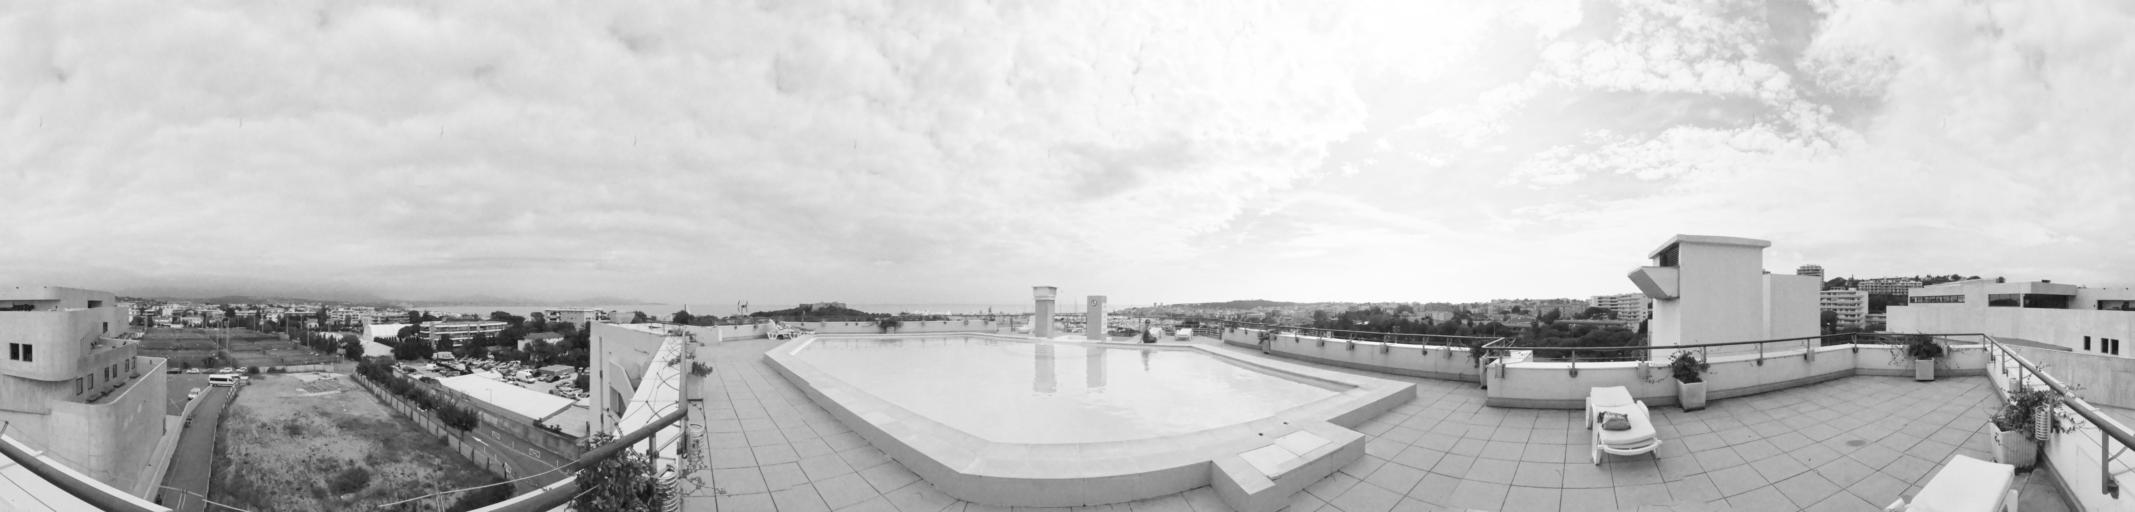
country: FR
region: Provence-Alpes-Cote d'Azur
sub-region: Departement des Alpes-Maritimes
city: Antibes
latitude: 43.5900
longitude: 7.1188
